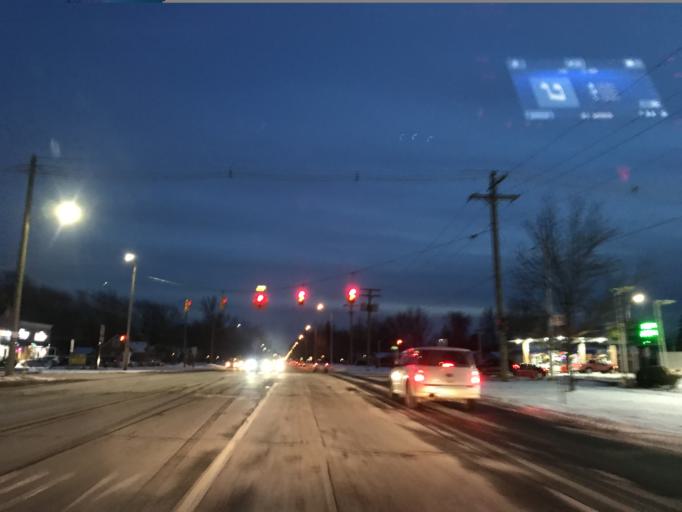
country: US
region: Michigan
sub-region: Wayne County
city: Redford
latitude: 42.3992
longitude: -83.3150
